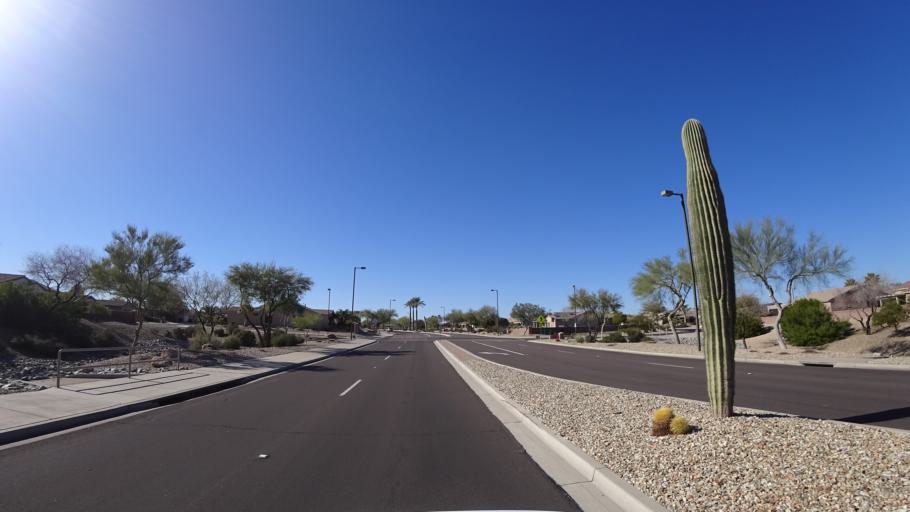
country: US
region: Arizona
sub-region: Maricopa County
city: Sun City West
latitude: 33.6724
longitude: -112.4132
